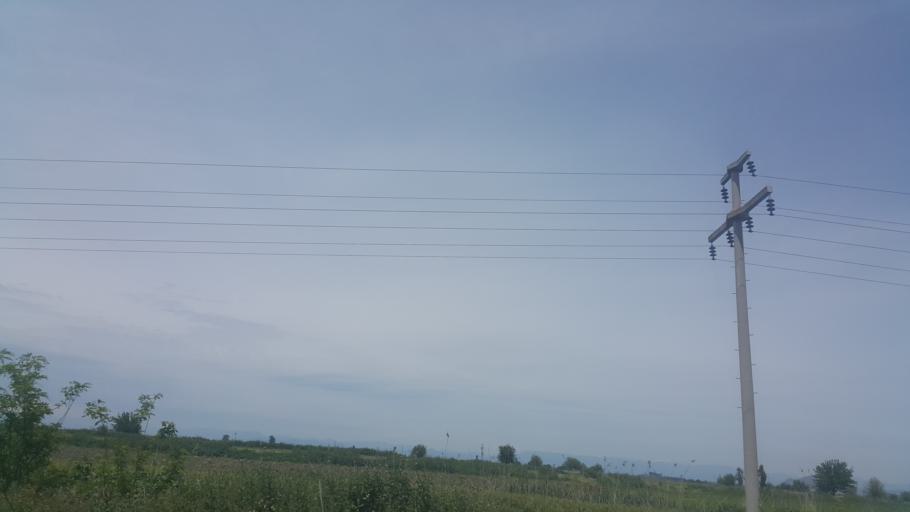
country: TR
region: Osmaniye
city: Toprakkale
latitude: 37.0730
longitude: 36.0414
